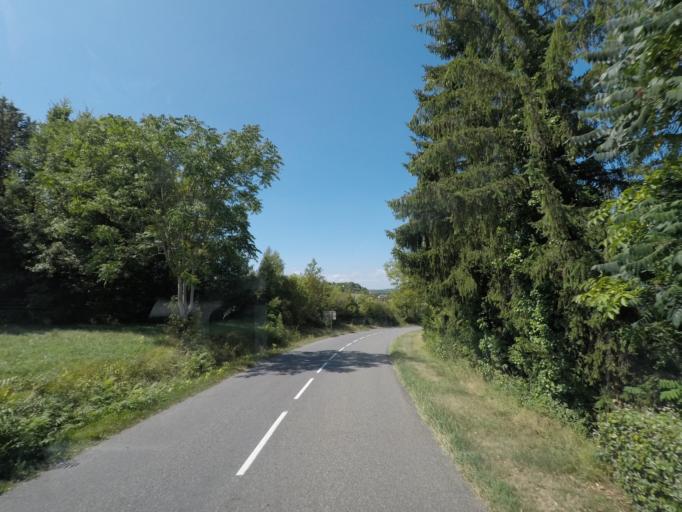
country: FR
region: Midi-Pyrenees
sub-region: Departement du Lot
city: Figeac
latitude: 44.6052
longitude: 2.0593
